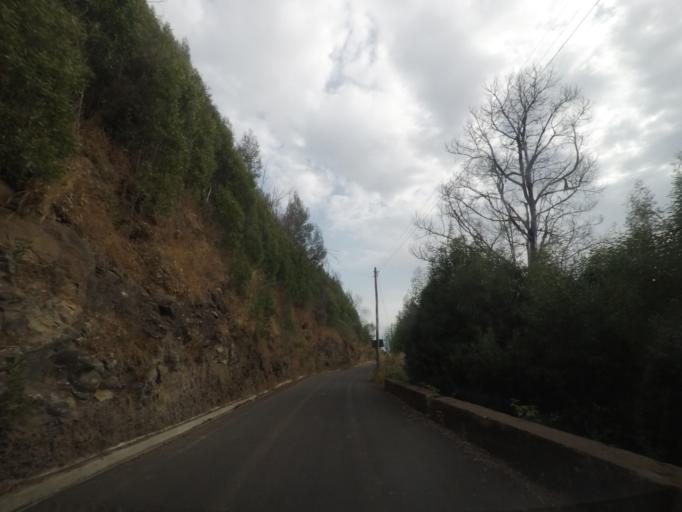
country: PT
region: Madeira
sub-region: Calheta
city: Arco da Calheta
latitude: 32.7383
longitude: -17.1536
